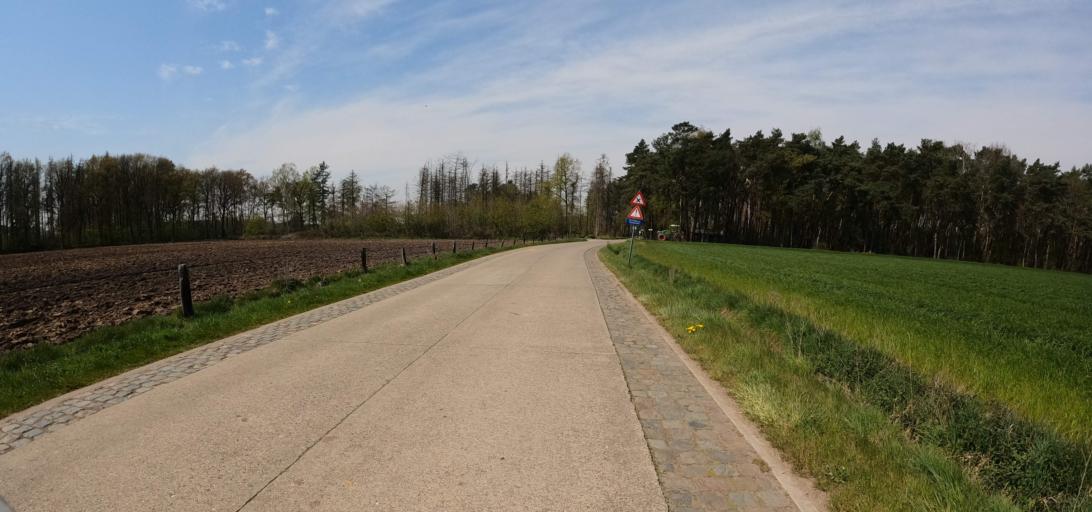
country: BE
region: Flanders
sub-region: Provincie Antwerpen
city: Vorselaar
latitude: 51.2381
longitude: 4.7643
